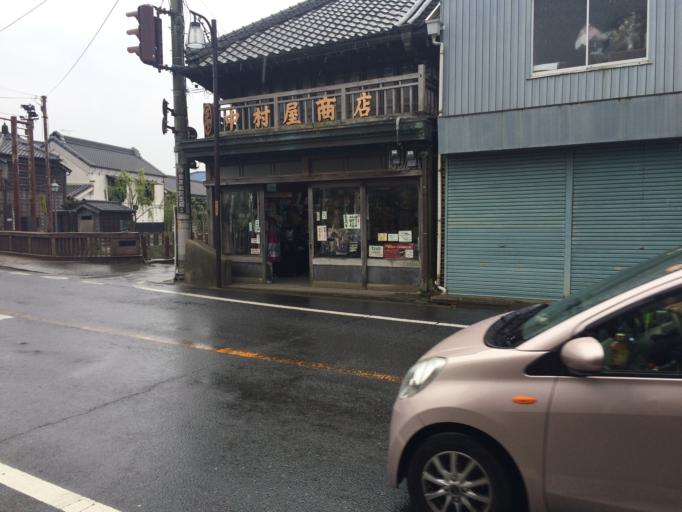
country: JP
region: Chiba
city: Sawara
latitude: 35.8891
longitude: 140.4979
